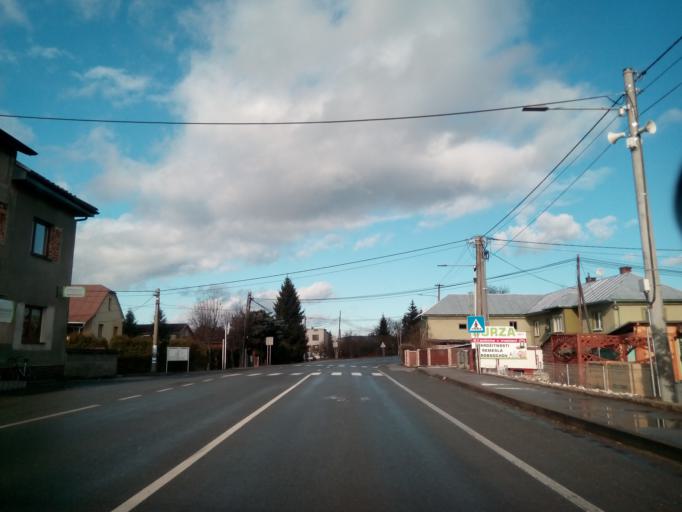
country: SK
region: Presovsky
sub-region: Okres Bardejov
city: Bardejov
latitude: 49.2138
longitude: 21.2966
